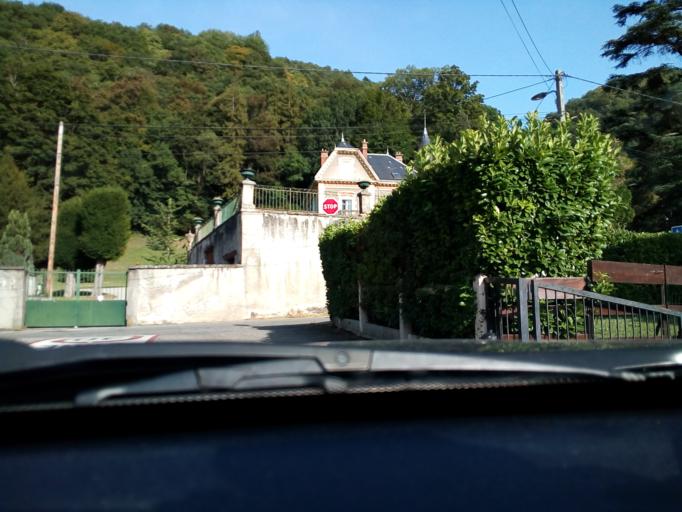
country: FR
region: Rhone-Alpes
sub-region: Departement de l'Isere
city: Saint-Martin-d'Heres
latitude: 45.1670
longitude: 5.7683
